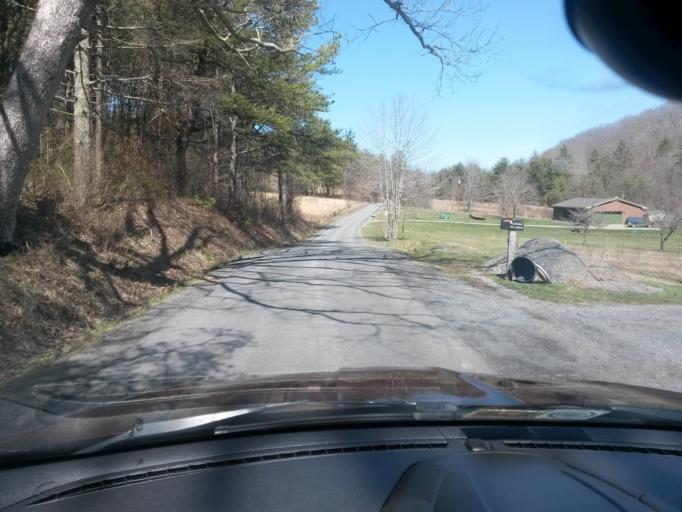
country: US
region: West Virginia
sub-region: Greenbrier County
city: White Sulphur Springs
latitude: 37.6527
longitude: -80.3250
